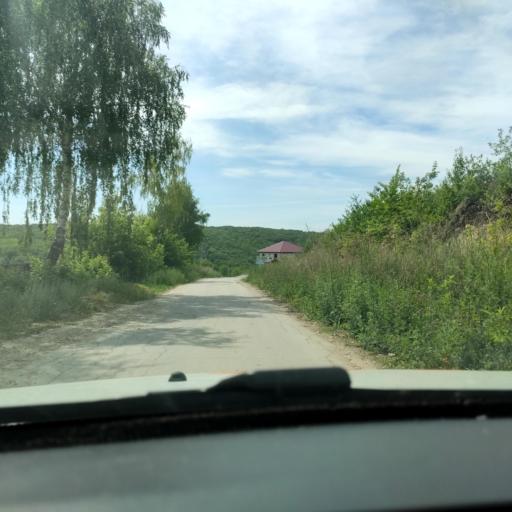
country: RU
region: Samara
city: Volzhskiy
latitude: 53.3403
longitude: 50.2001
